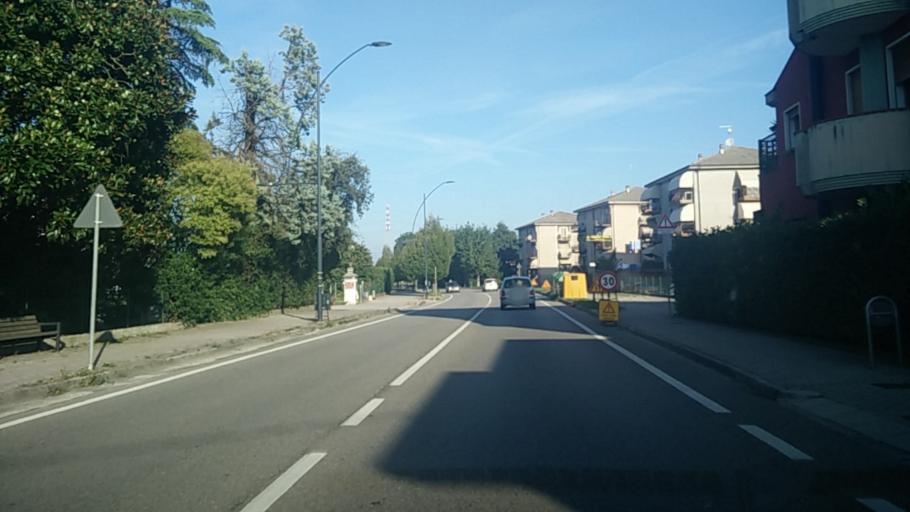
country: IT
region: Veneto
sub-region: Provincia di Venezia
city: Trivignano
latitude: 45.5303
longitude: 12.1862
